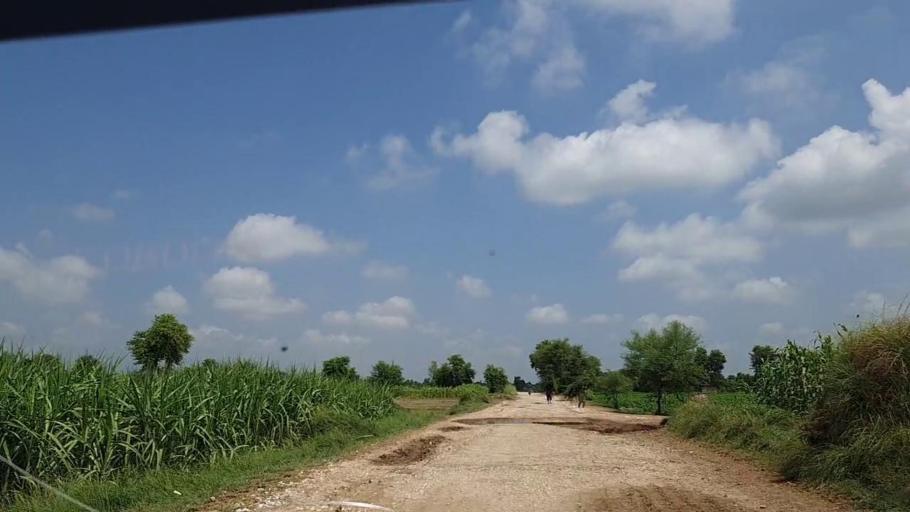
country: PK
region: Sindh
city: Tharu Shah
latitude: 26.9012
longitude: 68.0391
